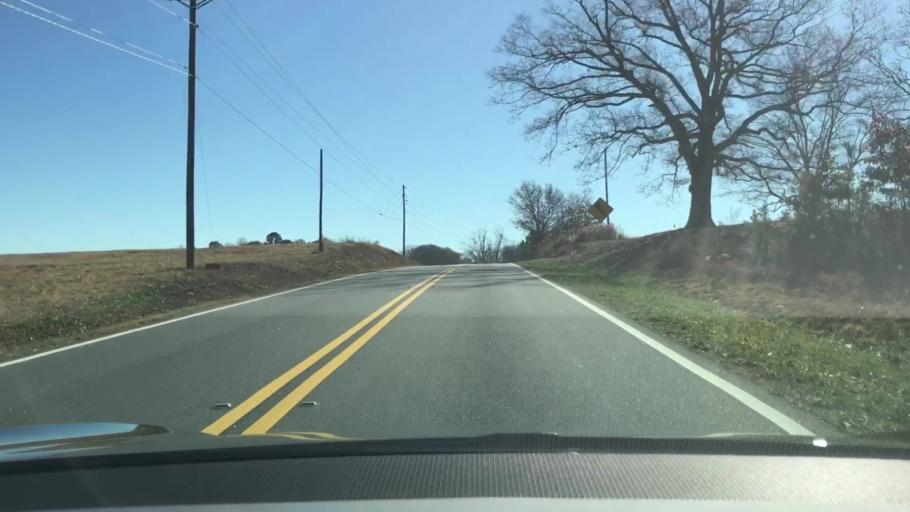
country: US
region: Georgia
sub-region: Walton County
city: Monroe
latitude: 33.8854
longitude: -83.7781
